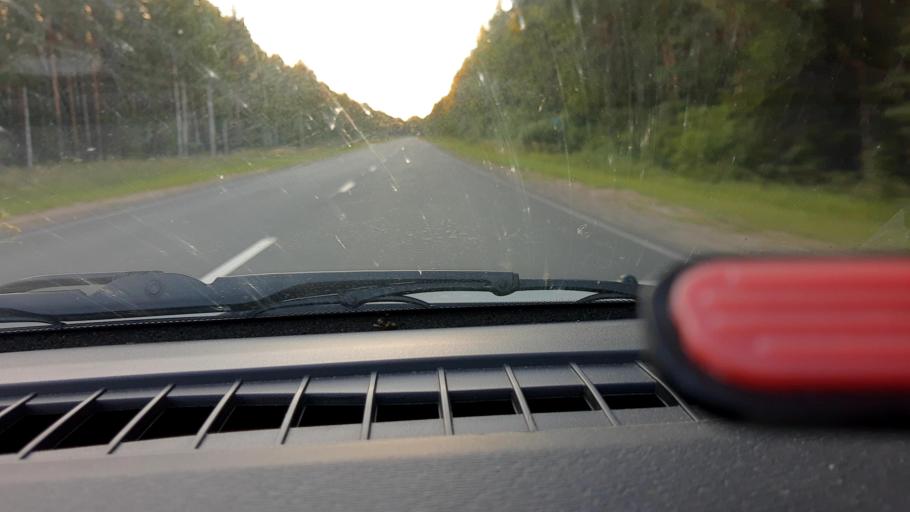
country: RU
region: Nizjnij Novgorod
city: Uren'
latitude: 57.3798
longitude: 45.6900
